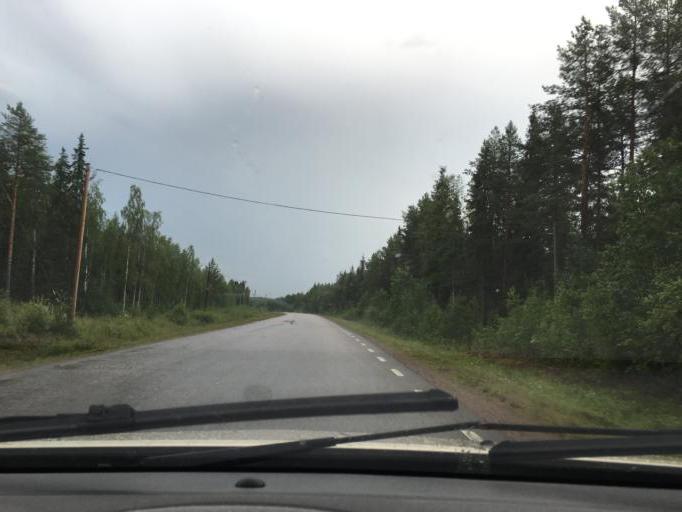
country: SE
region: Norrbotten
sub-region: Kalix Kommun
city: Toere
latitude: 66.0680
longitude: 22.7499
